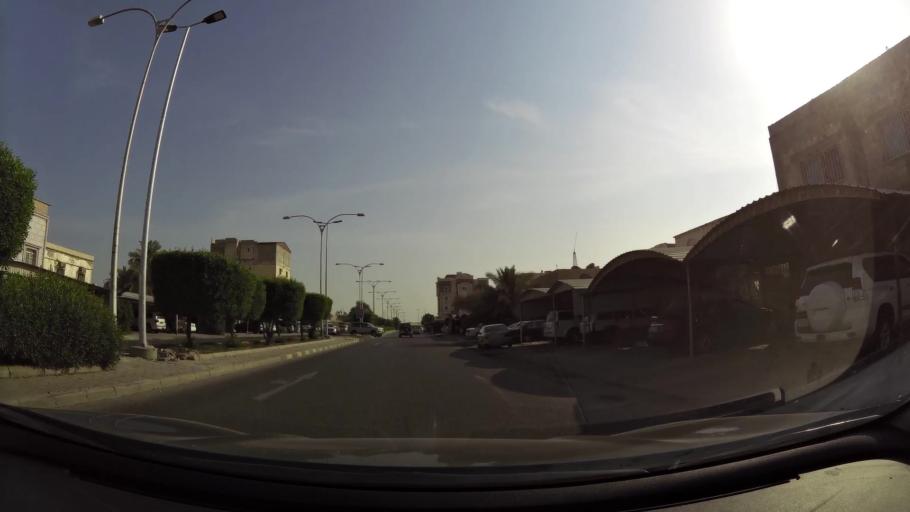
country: KW
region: Al Ahmadi
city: Ar Riqqah
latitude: 29.1387
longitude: 48.1083
